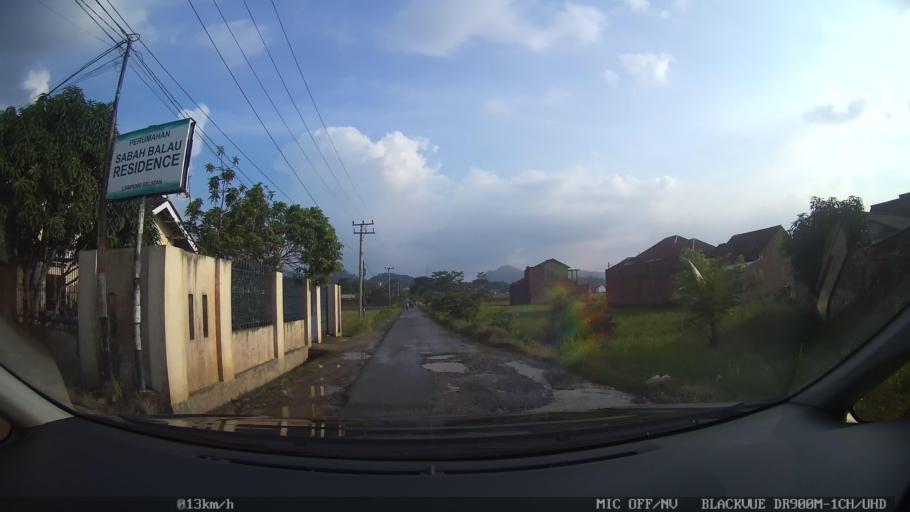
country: ID
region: Lampung
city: Kedaton
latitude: -5.3893
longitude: 105.3238
